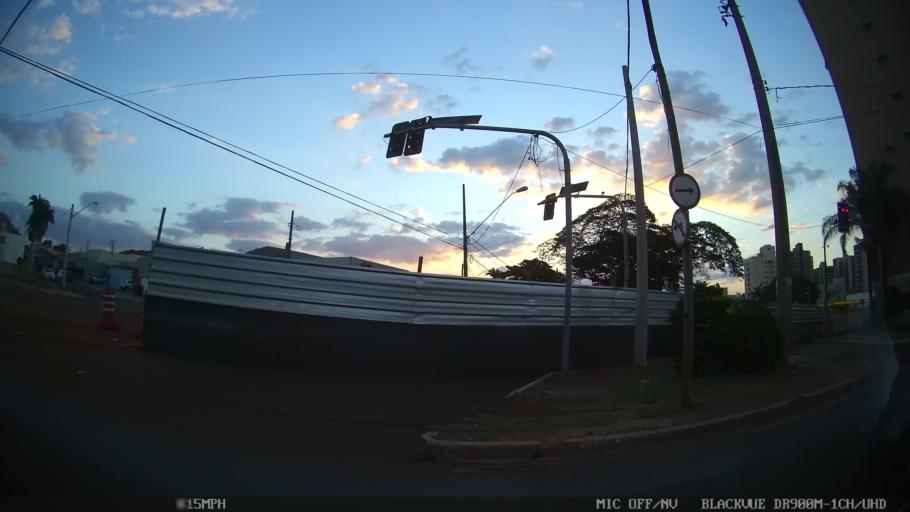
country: BR
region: Sao Paulo
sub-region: Ribeirao Preto
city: Ribeirao Preto
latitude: -21.1888
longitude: -47.8064
